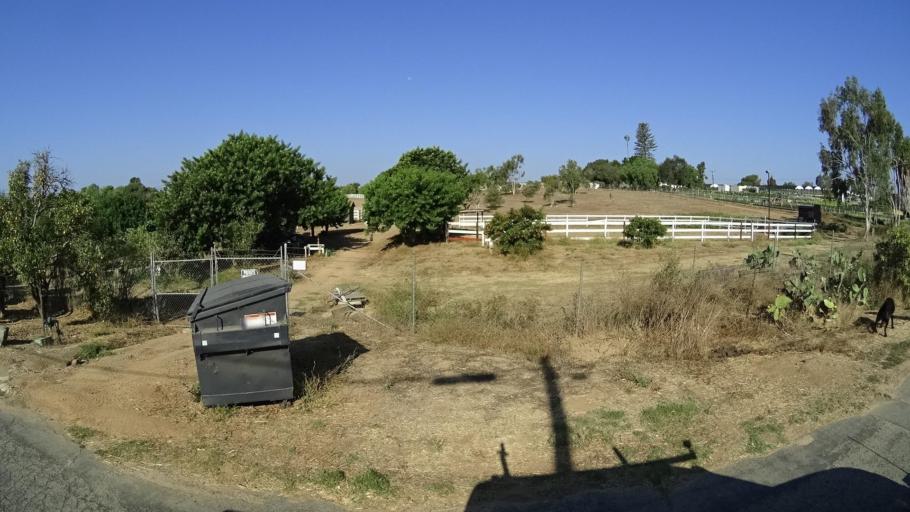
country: US
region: California
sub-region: San Diego County
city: Bonsall
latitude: 33.3226
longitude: -117.2600
